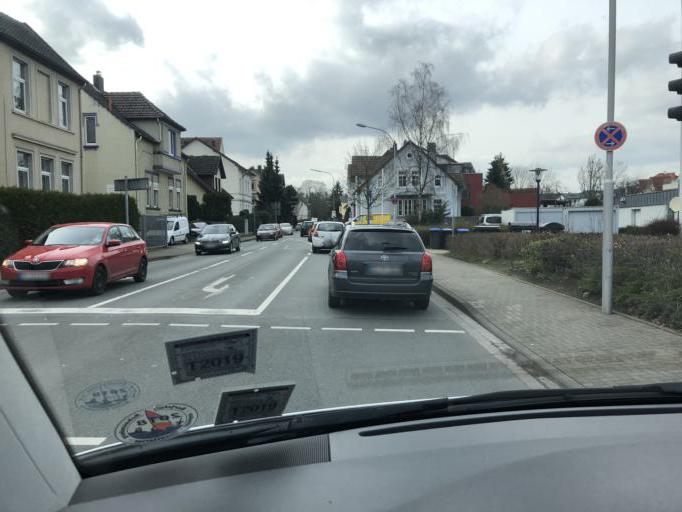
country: DE
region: North Rhine-Westphalia
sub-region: Regierungsbezirk Detmold
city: Herford
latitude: 52.1099
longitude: 8.6730
